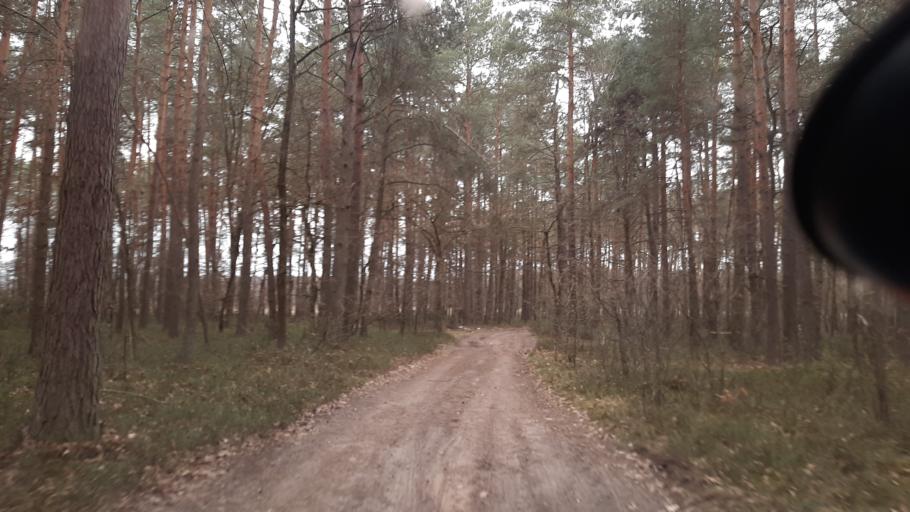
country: PL
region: Lublin Voivodeship
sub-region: Powiat lubartowski
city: Abramow
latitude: 51.4330
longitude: 22.3427
